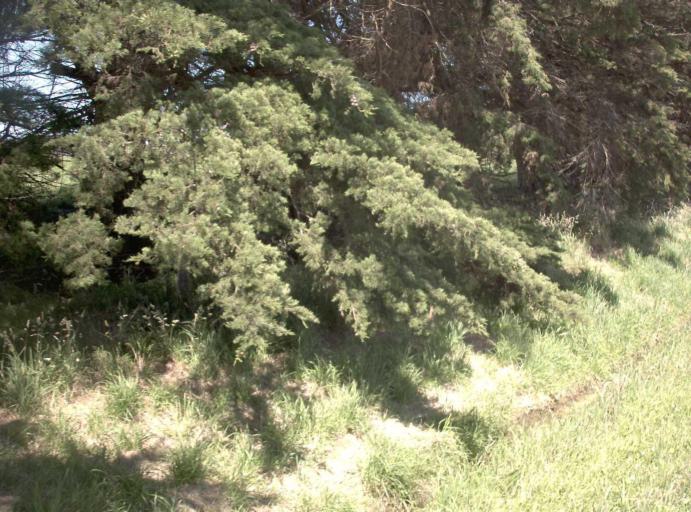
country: AU
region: Victoria
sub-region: Bass Coast
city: North Wonthaggi
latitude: -38.7448
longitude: 146.0733
